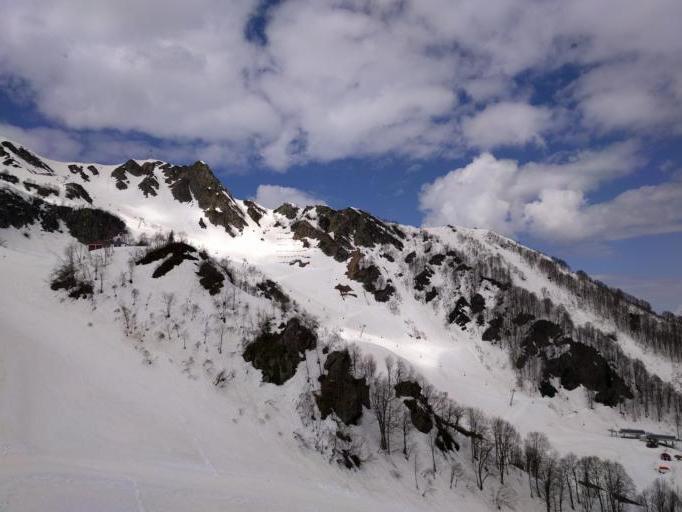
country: RU
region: Krasnodarskiy
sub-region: Sochi City
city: Krasnaya Polyana
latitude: 43.6319
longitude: 40.3119
